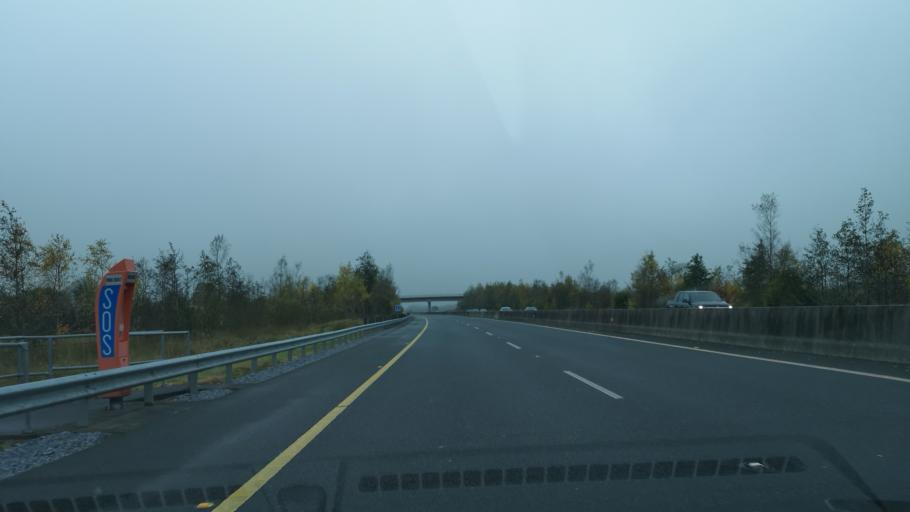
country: IE
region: Connaught
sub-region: County Galway
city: Ballinasloe
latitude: 53.3007
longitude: -8.3413
